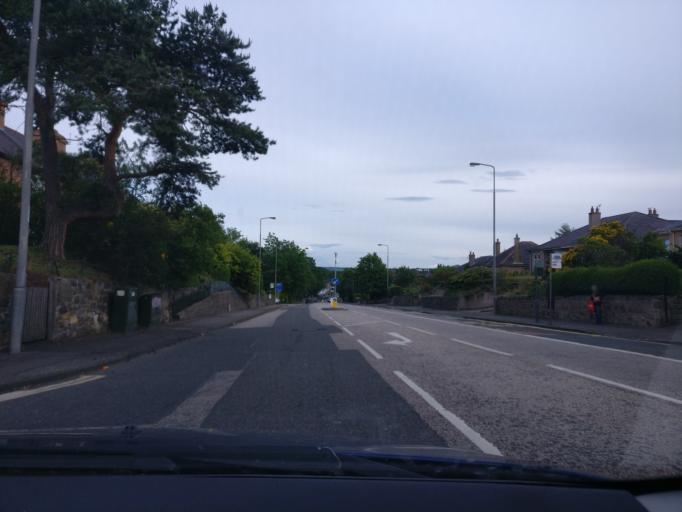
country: GB
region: Scotland
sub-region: West Lothian
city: Seafield
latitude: 55.9498
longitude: -3.1400
